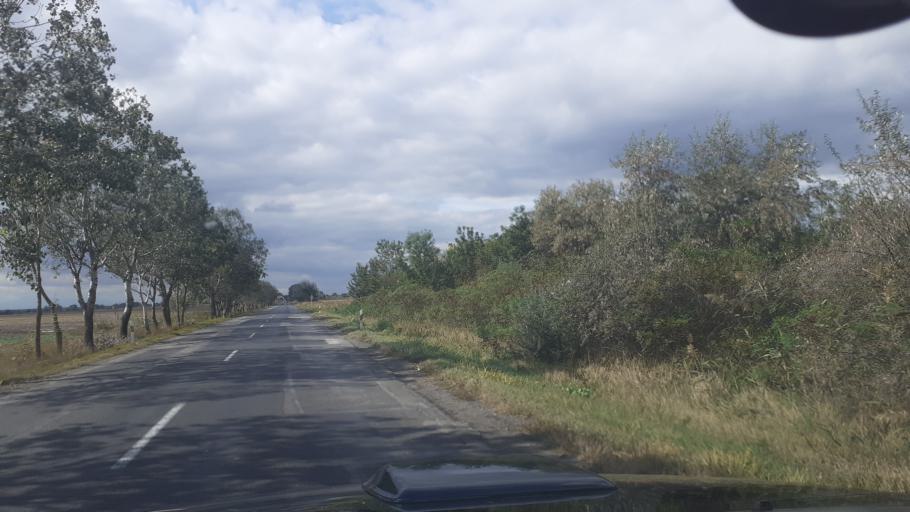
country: HU
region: Bacs-Kiskun
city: Solt
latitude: 46.7977
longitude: 19.0634
